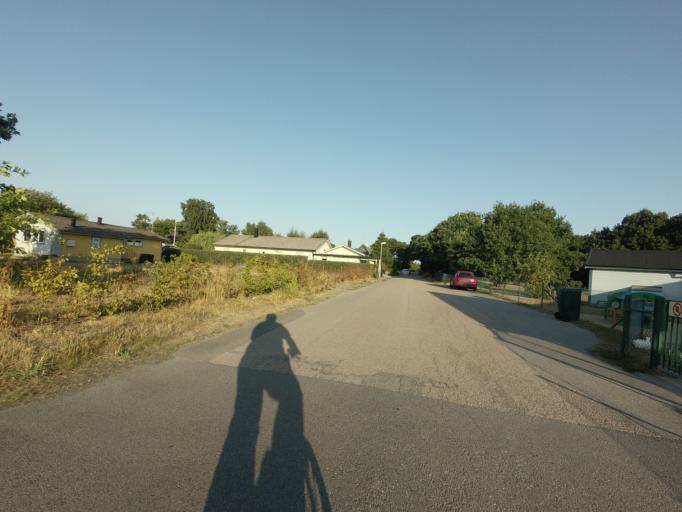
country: SE
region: Skane
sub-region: Hoganas Kommun
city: Hoganas
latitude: 56.1532
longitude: 12.5731
